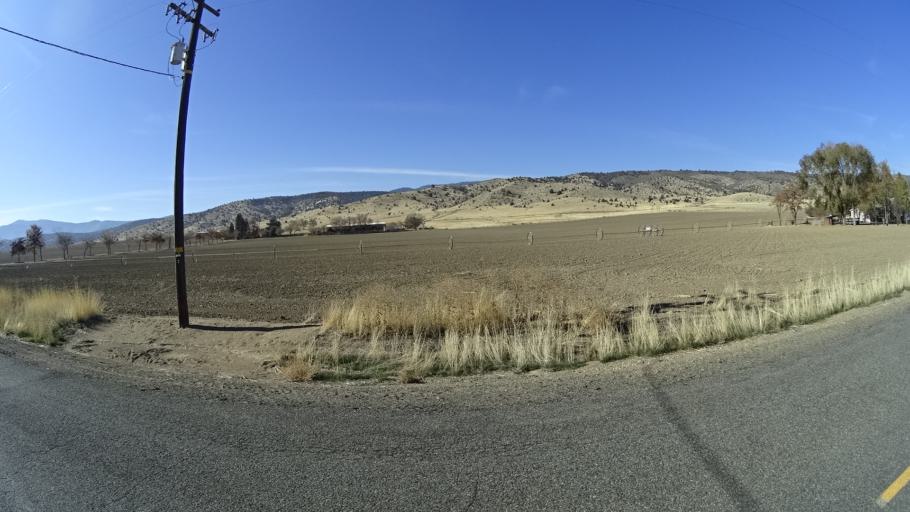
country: US
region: California
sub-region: Siskiyou County
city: Montague
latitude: 41.5731
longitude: -122.5481
